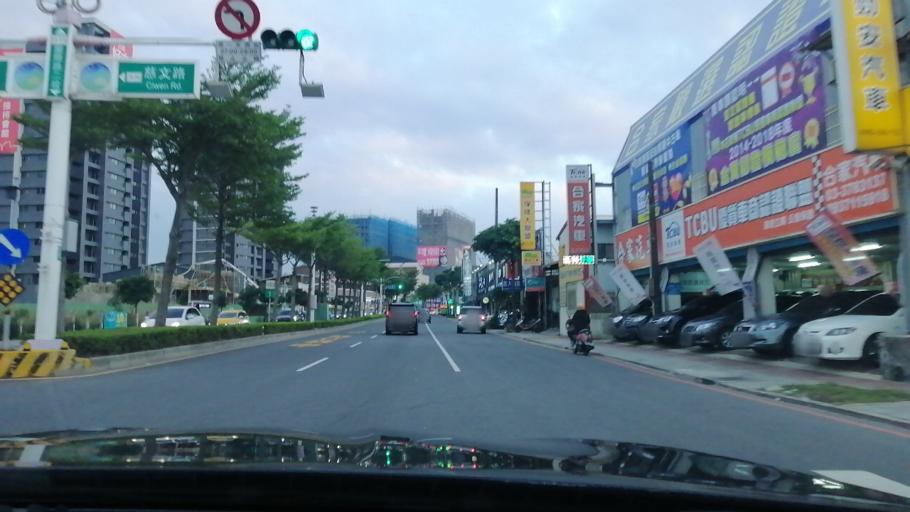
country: TW
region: Taiwan
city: Taoyuan City
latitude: 25.0003
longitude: 121.2875
